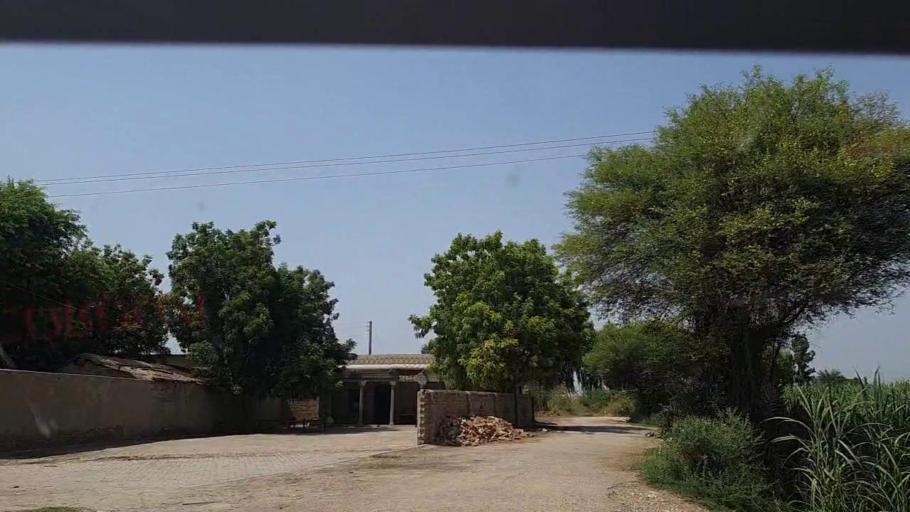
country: PK
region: Sindh
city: Ghotki
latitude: 28.0713
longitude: 69.3175
